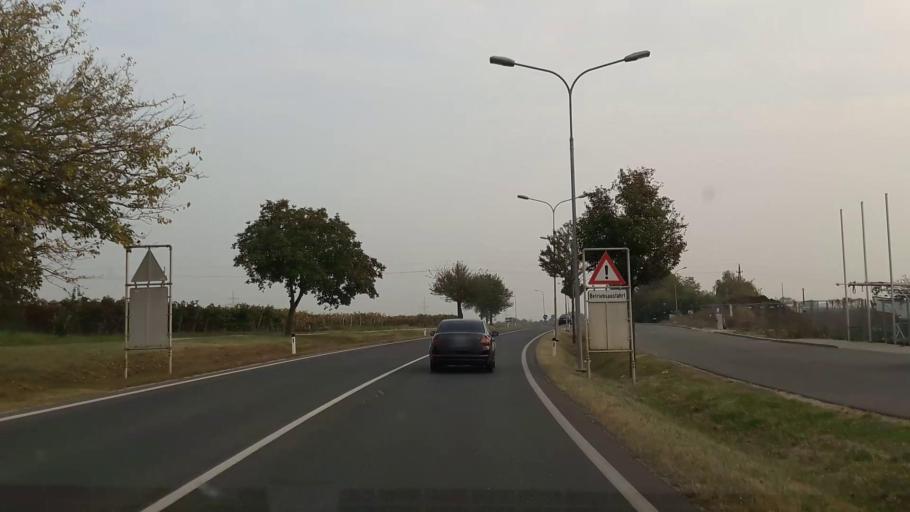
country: AT
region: Burgenland
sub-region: Politischer Bezirk Neusiedl am See
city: Weiden am See
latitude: 47.9206
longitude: 16.8775
